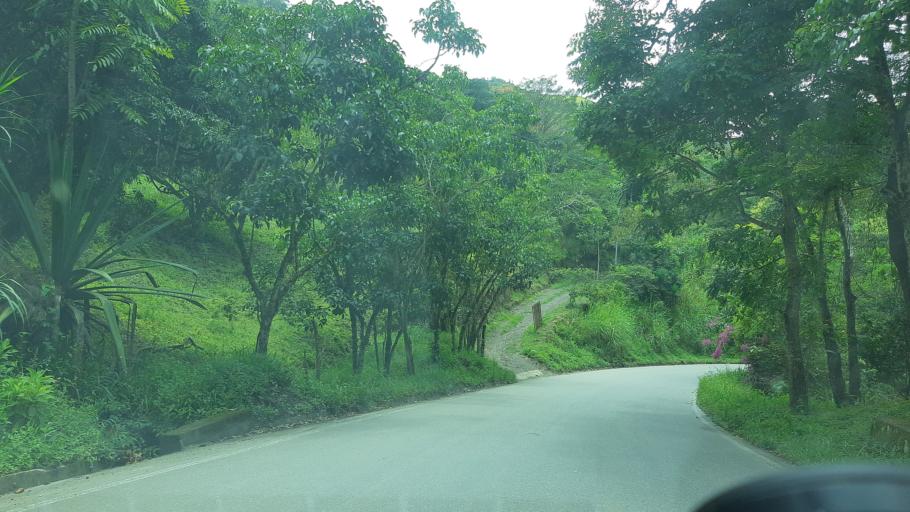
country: CO
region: Cundinamarca
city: Tenza
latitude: 5.0283
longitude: -73.3897
